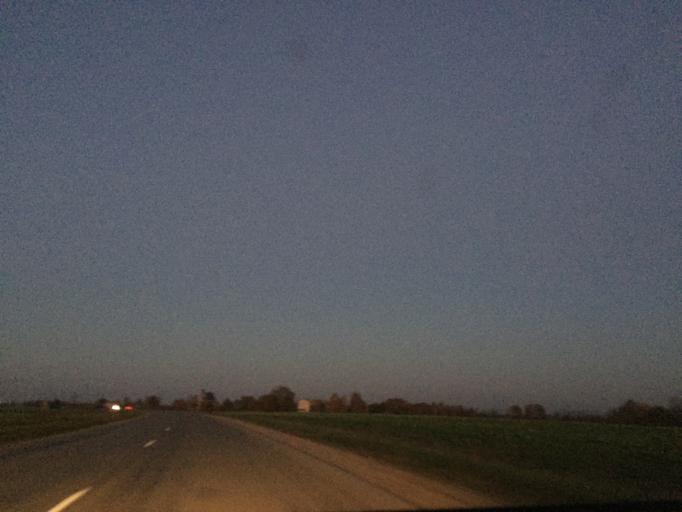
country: LV
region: Tervete
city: Zelmeni
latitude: 56.4997
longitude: 23.2598
